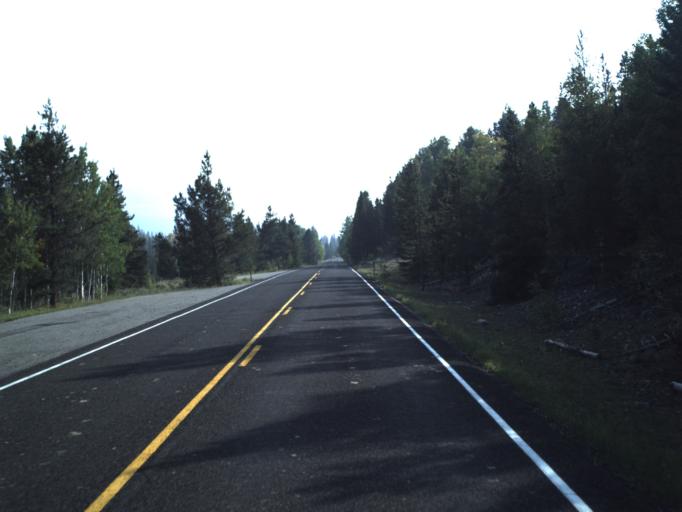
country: US
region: Wyoming
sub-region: Uinta County
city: Evanston
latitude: 40.8365
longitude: -110.8495
